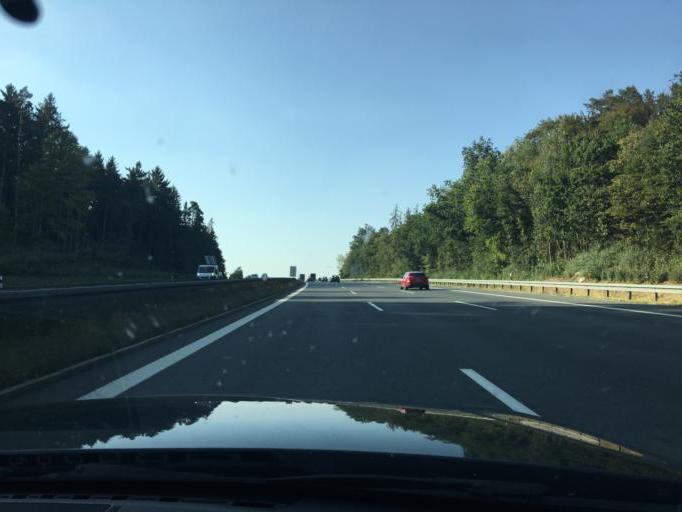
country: DE
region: Bavaria
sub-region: Upper Bavaria
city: Denkendorf
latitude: 48.9394
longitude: 11.4513
